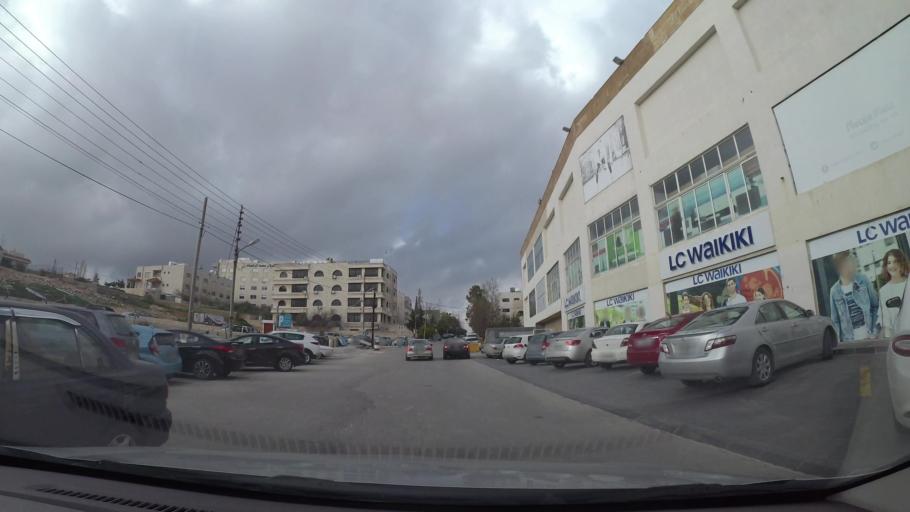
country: JO
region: Amman
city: Wadi as Sir
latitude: 31.9782
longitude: 35.8433
